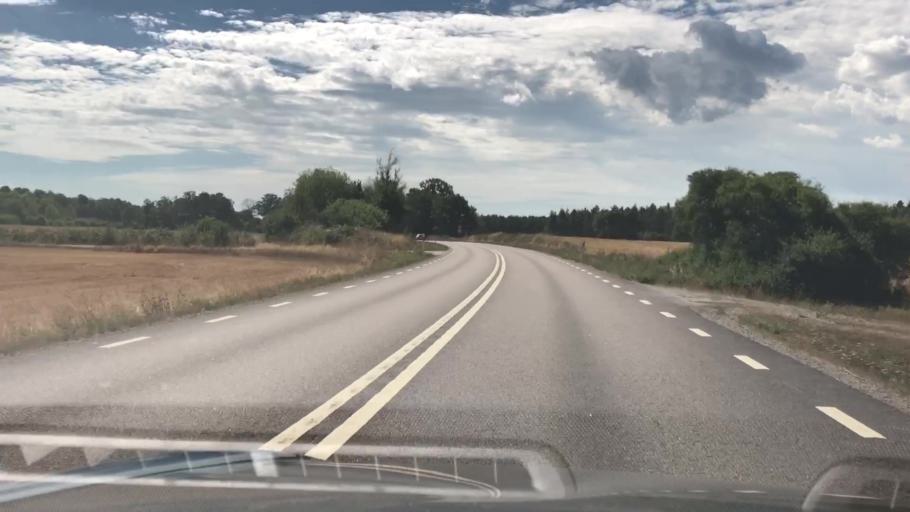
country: SE
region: Kalmar
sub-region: Torsas Kommun
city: Torsas
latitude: 56.4181
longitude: 16.0677
